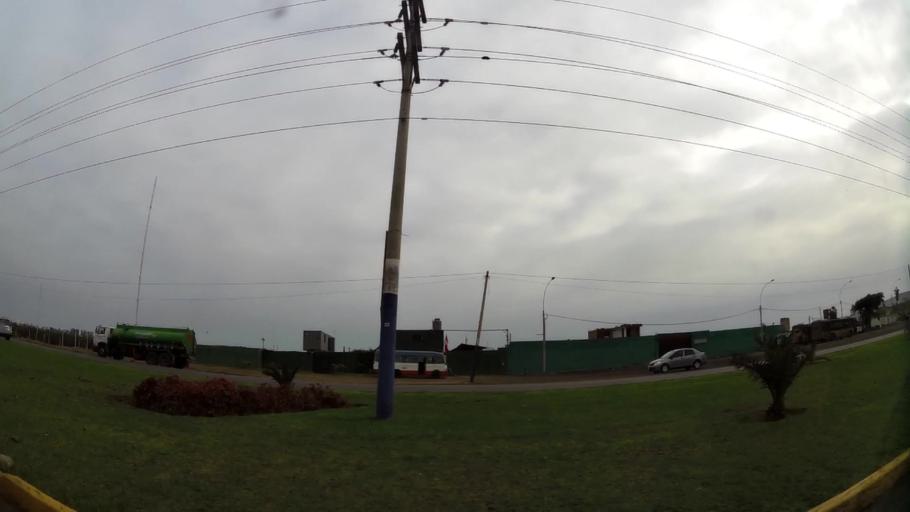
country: PE
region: Lima
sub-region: Lima
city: Surco
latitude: -12.2011
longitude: -76.9955
